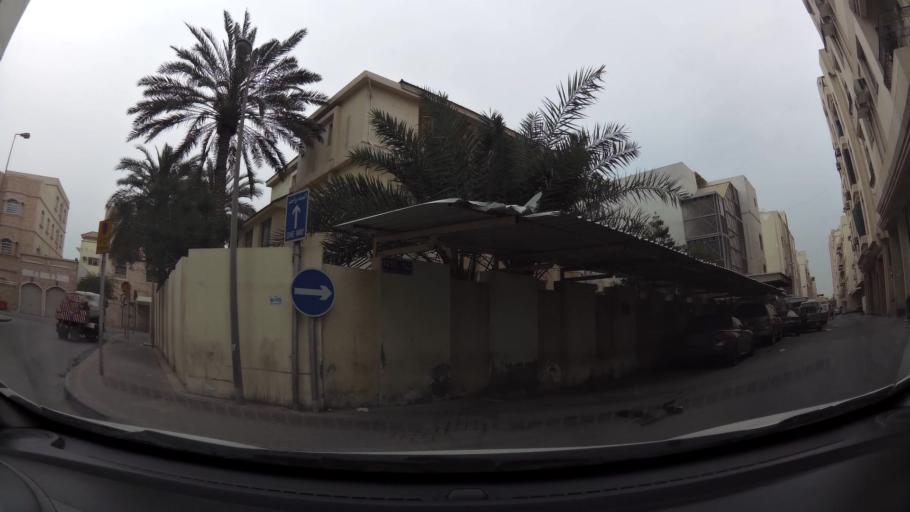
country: BH
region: Manama
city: Jidd Hafs
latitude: 26.2243
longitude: 50.5652
